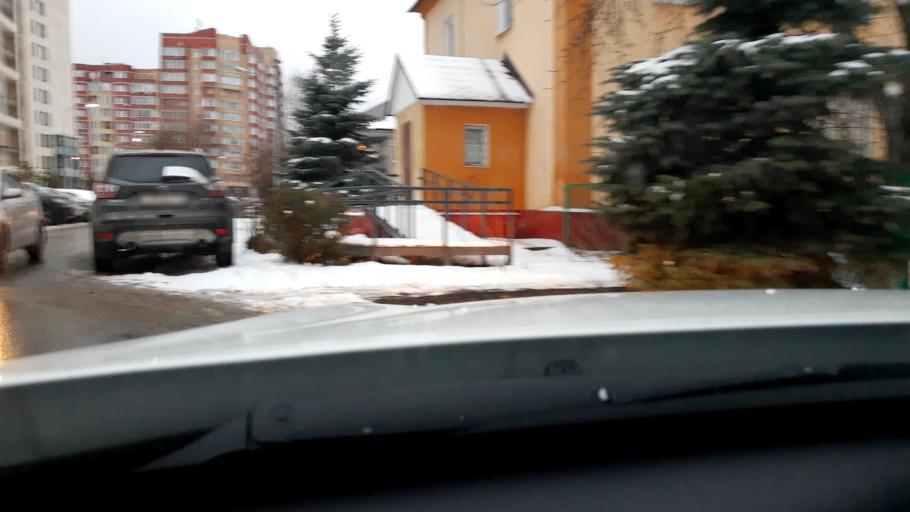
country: RU
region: Moskovskaya
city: Krasnogorsk
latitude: 55.8746
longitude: 37.3155
